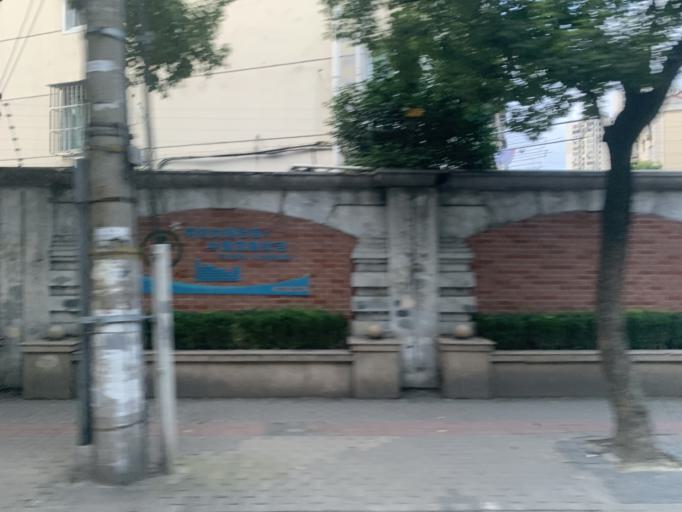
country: CN
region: Shanghai Shi
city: Pudong
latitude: 31.2479
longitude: 121.5492
